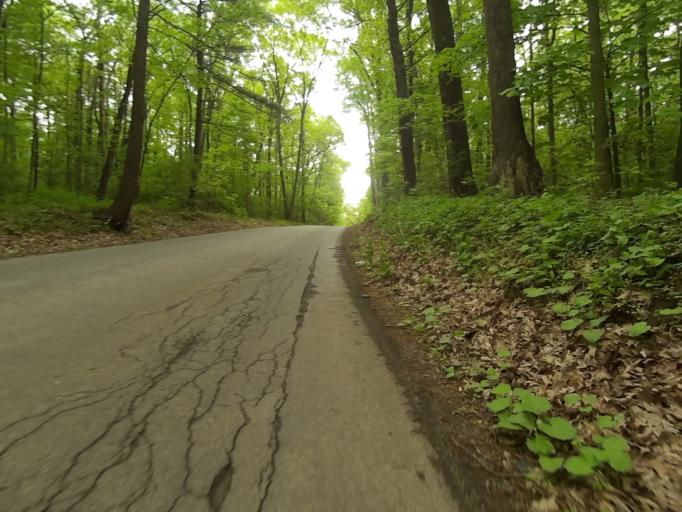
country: US
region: Pennsylvania
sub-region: Centre County
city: Zion
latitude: 40.9754
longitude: -77.6227
